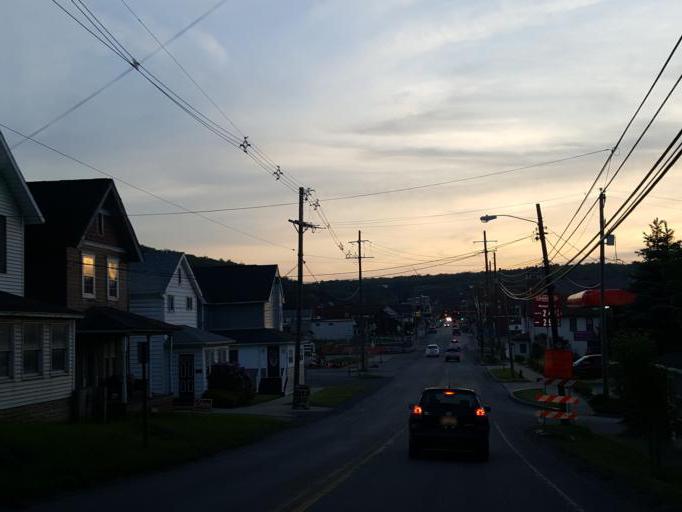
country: US
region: Pennsylvania
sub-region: Cambria County
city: Patton
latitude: 40.6339
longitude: -78.6448
